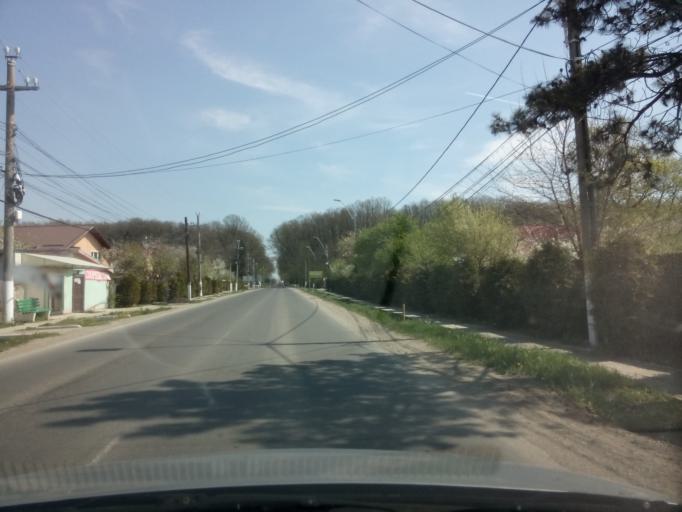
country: RO
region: Ilfov
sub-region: Comuna Corbeanca
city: Tamasi
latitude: 44.5866
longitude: 26.0174
